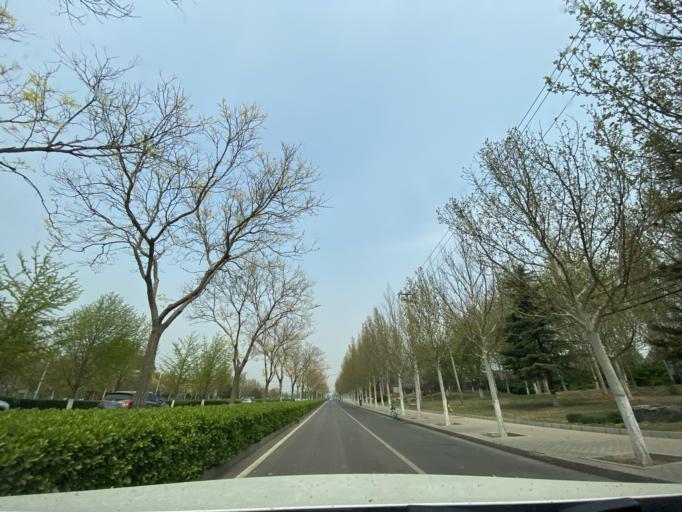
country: CN
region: Beijing
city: Sijiqing
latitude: 39.9434
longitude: 116.2411
